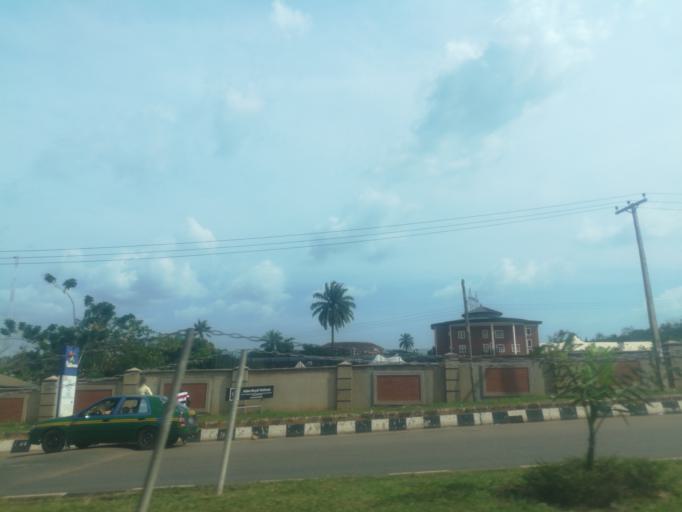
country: NG
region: Ogun
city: Abeokuta
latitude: 7.1274
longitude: 3.3582
